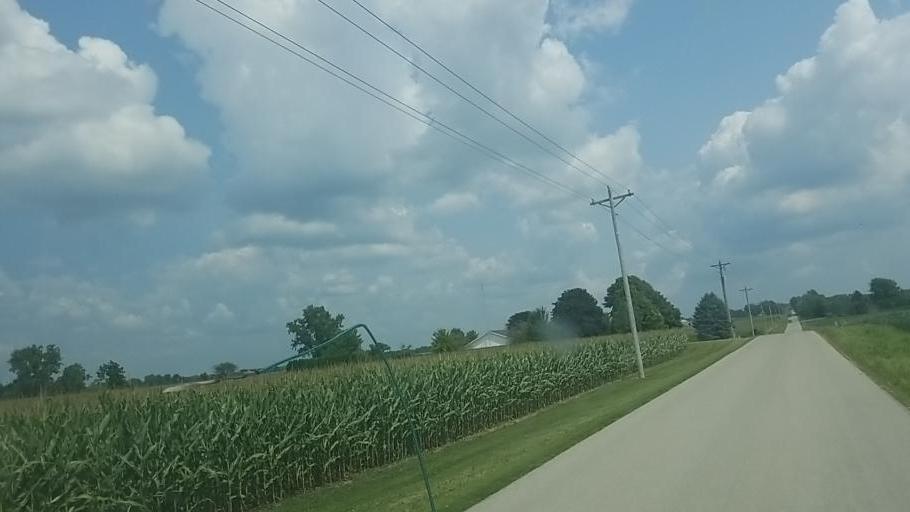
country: US
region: Ohio
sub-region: Wyandot County
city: Upper Sandusky
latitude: 40.9209
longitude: -83.1599
